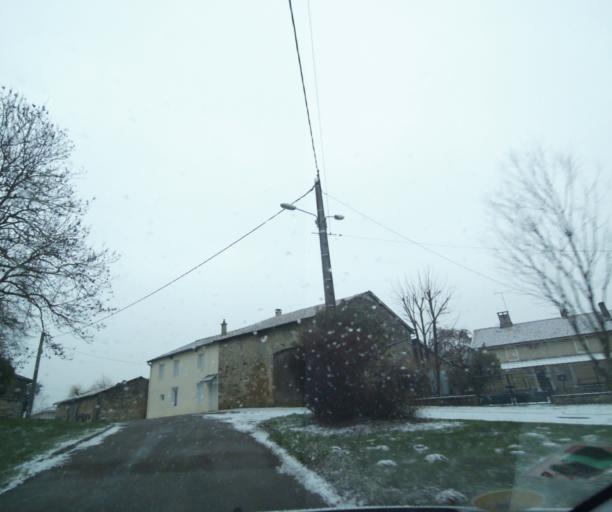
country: FR
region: Champagne-Ardenne
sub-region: Departement de la Haute-Marne
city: Wassy
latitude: 48.4608
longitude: 5.0305
